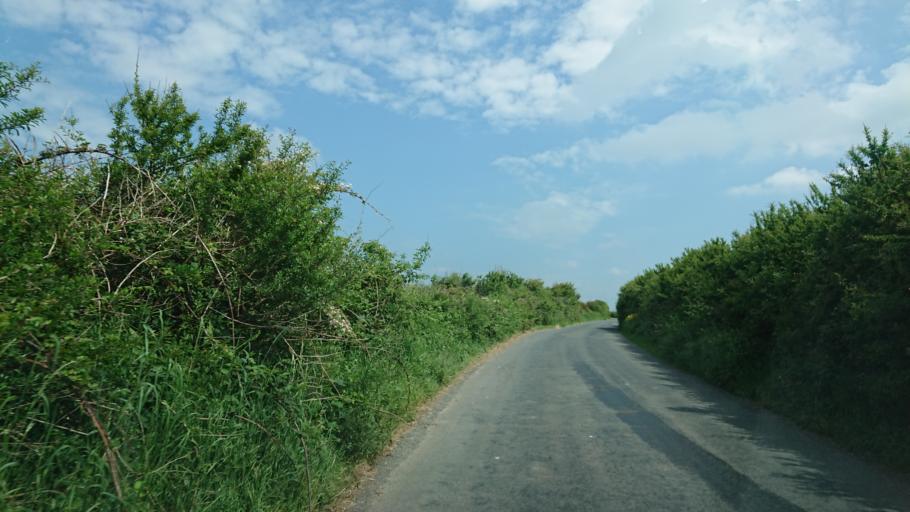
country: IE
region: Munster
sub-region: Waterford
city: Dunmore East
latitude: 52.2270
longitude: -7.0057
